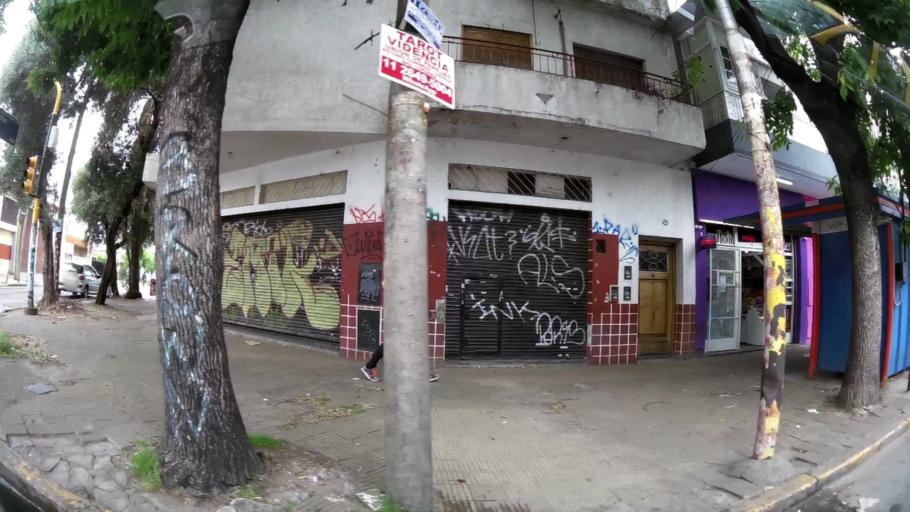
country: AR
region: Buenos Aires
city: San Justo
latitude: -34.6652
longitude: -58.5438
